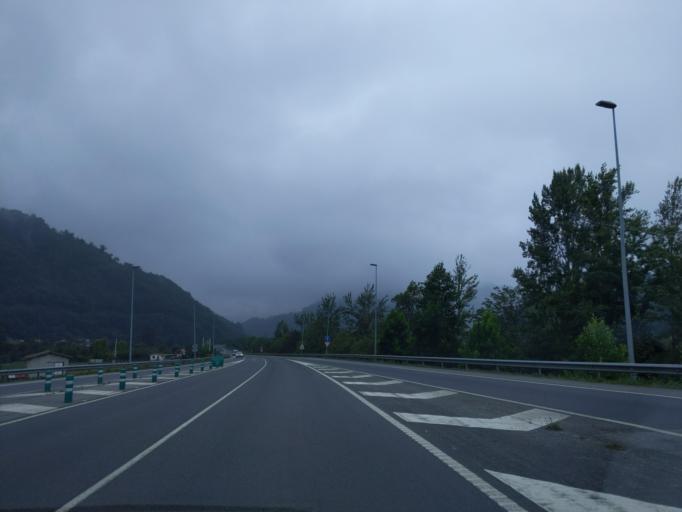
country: ES
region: Asturias
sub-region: Province of Asturias
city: Pola de Laviana
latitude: 43.2506
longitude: -5.5690
